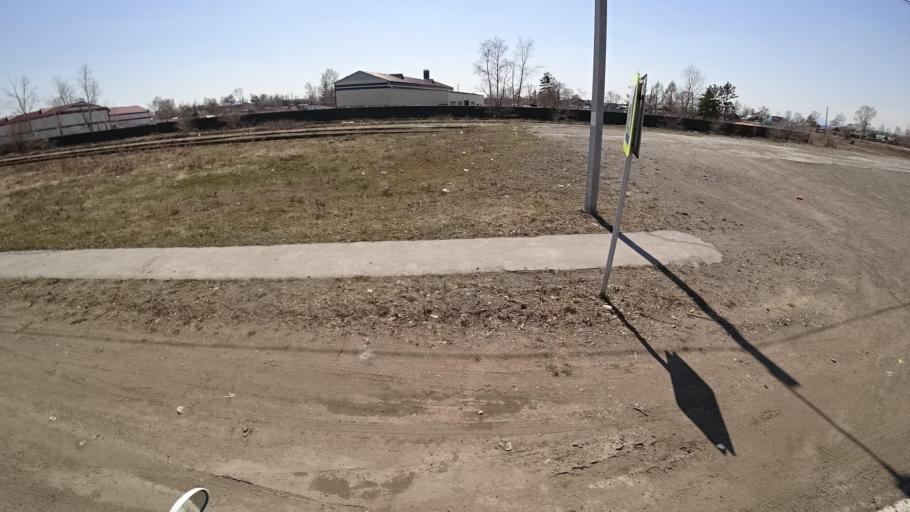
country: RU
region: Khabarovsk Krai
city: Khurba
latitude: 50.4093
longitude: 136.8889
